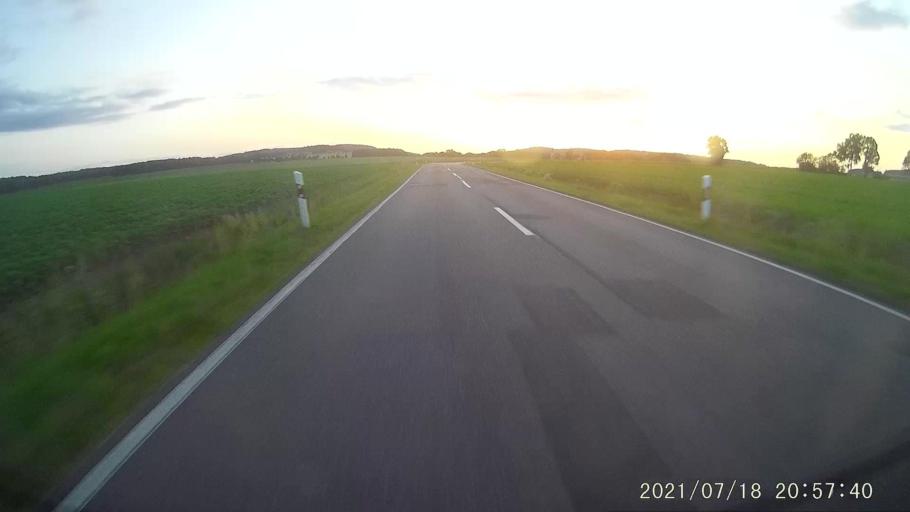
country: DE
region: Saxony
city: Konigshain
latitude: 51.1750
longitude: 14.9006
